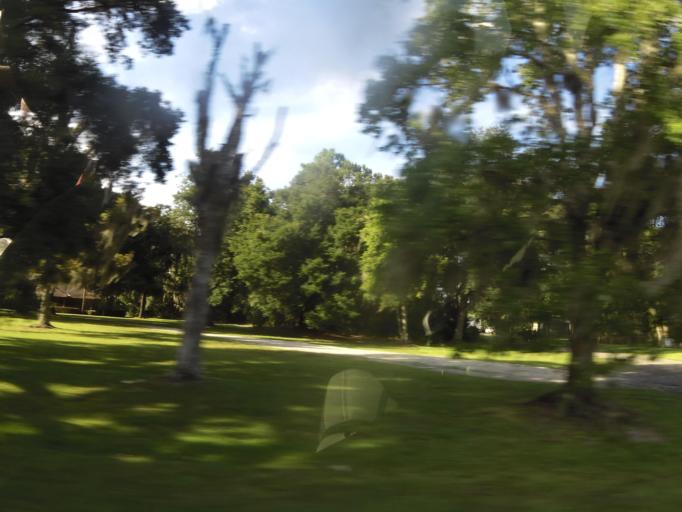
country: US
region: Florida
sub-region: Clay County
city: Green Cove Springs
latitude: 29.9177
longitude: -81.5712
